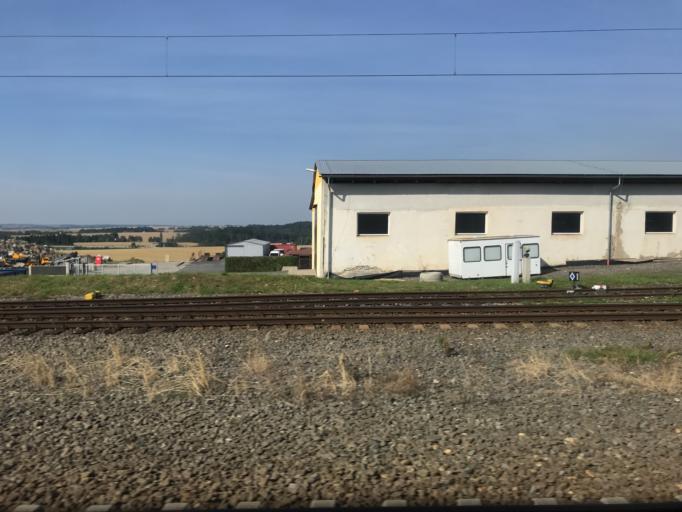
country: CZ
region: Jihocesky
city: Chotoviny
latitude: 49.4717
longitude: 14.6703
